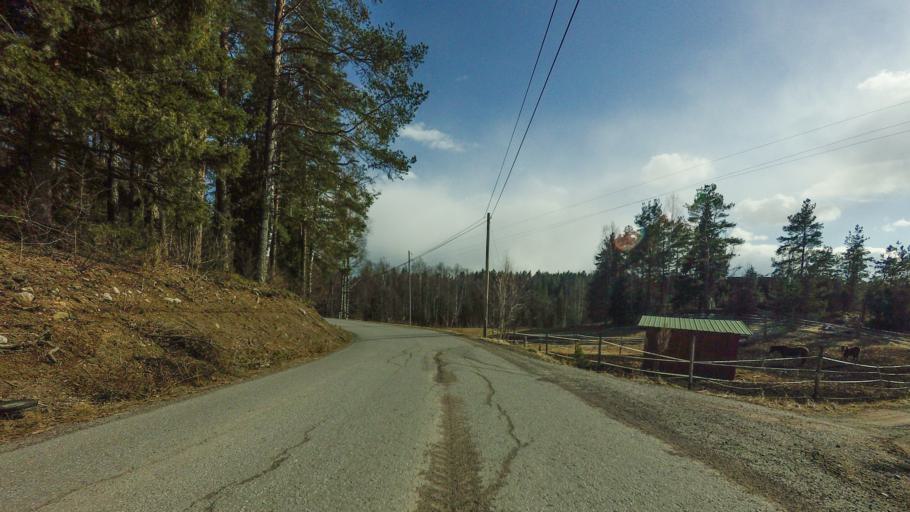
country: FI
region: Uusimaa
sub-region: Helsinki
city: Karjalohja
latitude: 60.2659
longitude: 23.6681
